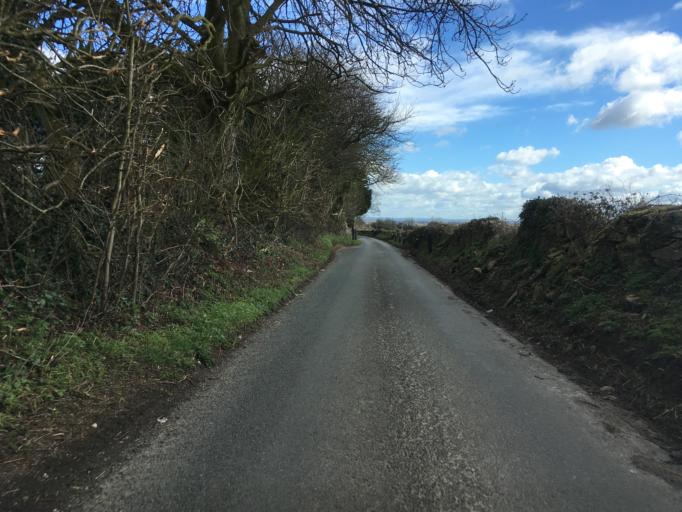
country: GB
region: England
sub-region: South Gloucestershire
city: Hinton
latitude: 51.5047
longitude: -2.3440
